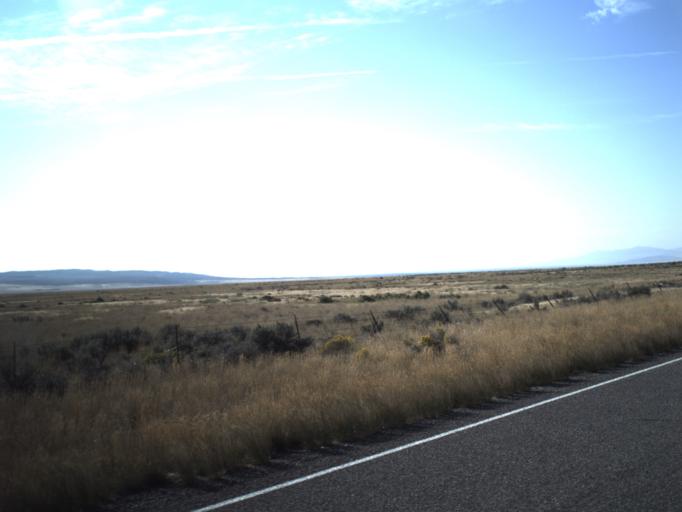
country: US
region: Idaho
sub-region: Oneida County
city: Malad City
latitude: 41.9159
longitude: -113.0979
